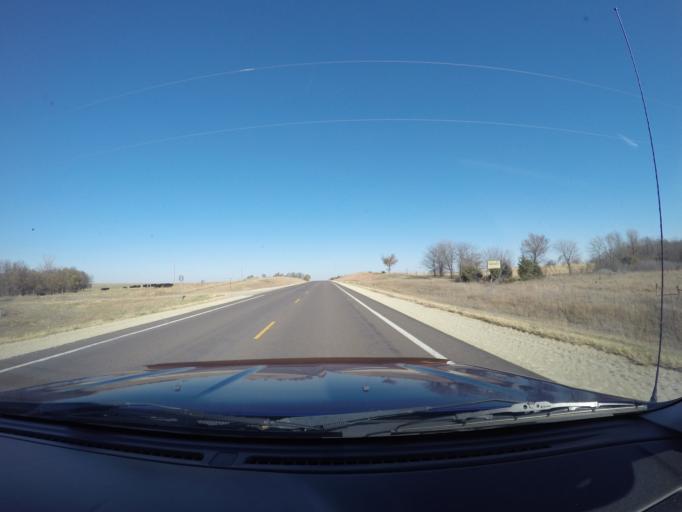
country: US
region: Kansas
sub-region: Marshall County
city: Blue Rapids
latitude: 39.6677
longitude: -96.7505
